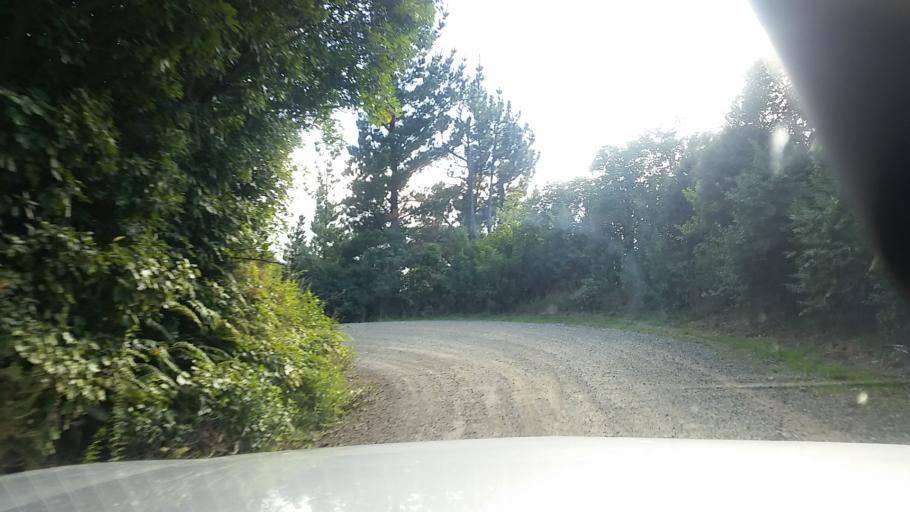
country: NZ
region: Marlborough
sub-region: Marlborough District
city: Picton
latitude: -41.2973
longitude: 174.1236
